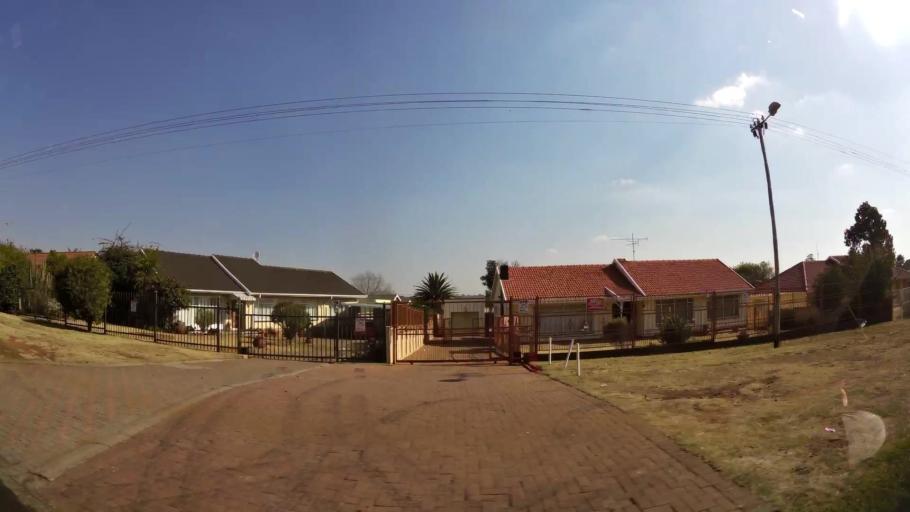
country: ZA
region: Gauteng
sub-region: West Rand District Municipality
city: Randfontein
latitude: -26.1627
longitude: 27.6947
